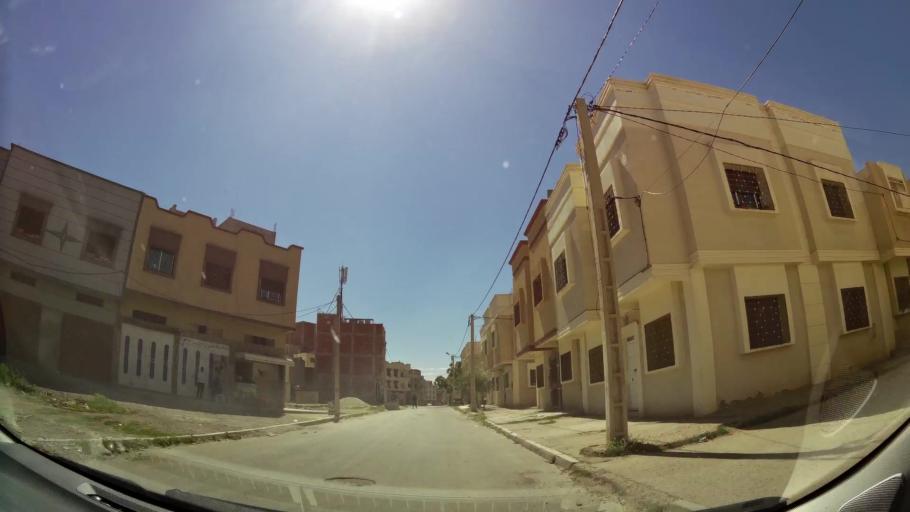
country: MA
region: Oriental
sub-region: Oujda-Angad
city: Oujda
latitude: 34.6572
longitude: -1.8755
